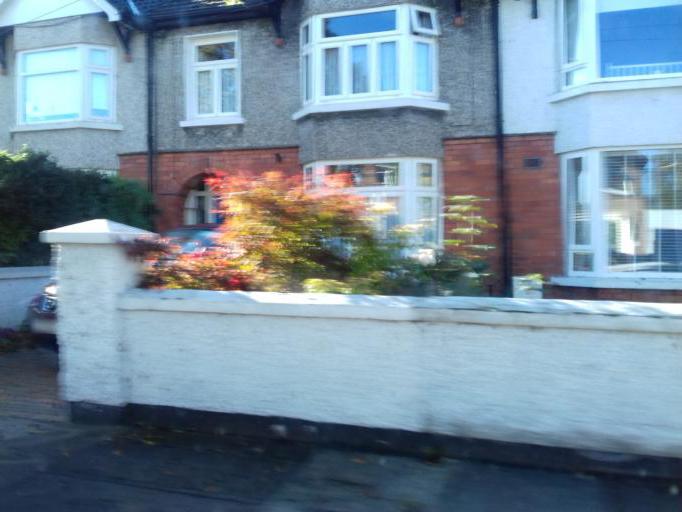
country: IE
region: Leinster
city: Cabra
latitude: 53.3635
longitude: -6.3068
